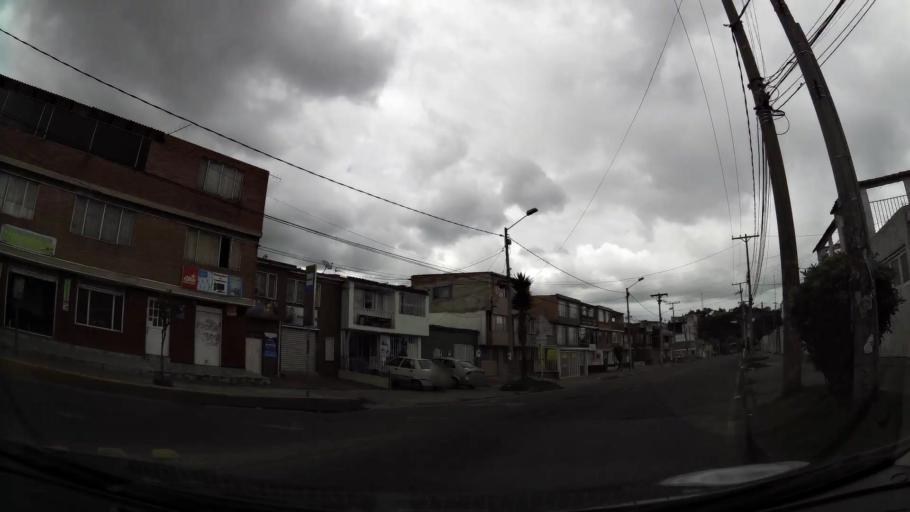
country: CO
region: Bogota D.C.
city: Barrio San Luis
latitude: 4.7068
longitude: -74.0925
